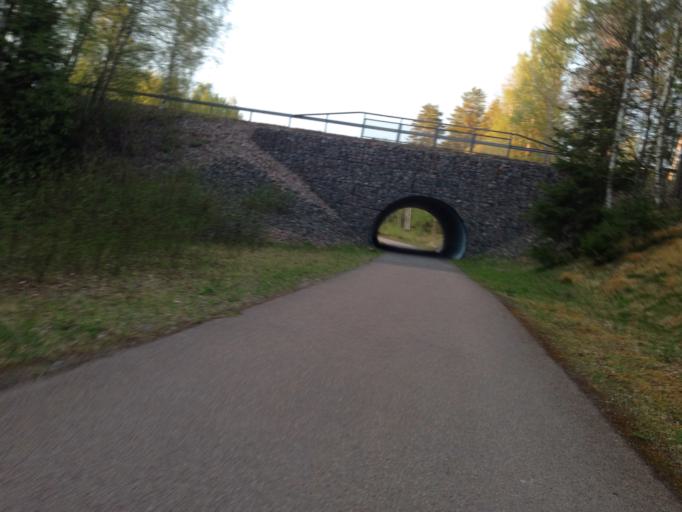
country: SE
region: Dalarna
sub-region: Ludvika Kommun
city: Grangesberg
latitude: 60.1243
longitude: 15.0680
